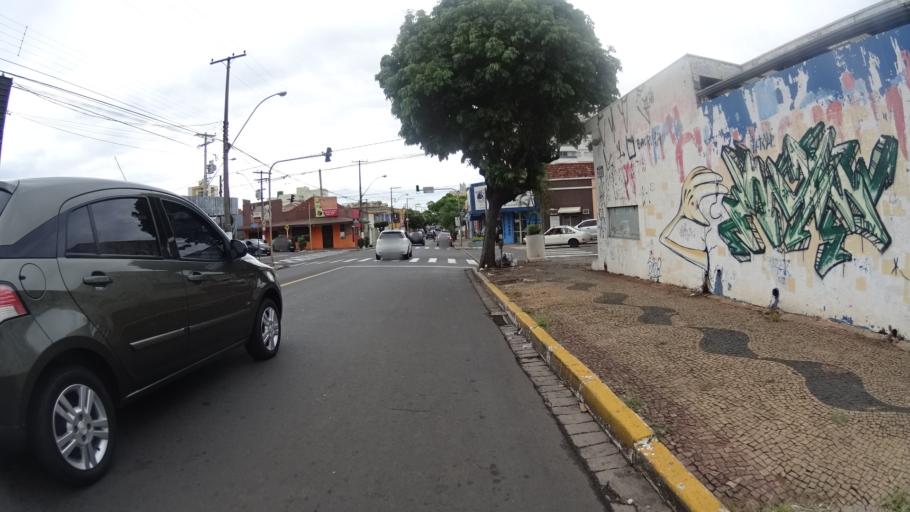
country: BR
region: Sao Paulo
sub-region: Marilia
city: Marilia
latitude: -22.2187
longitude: -49.9419
